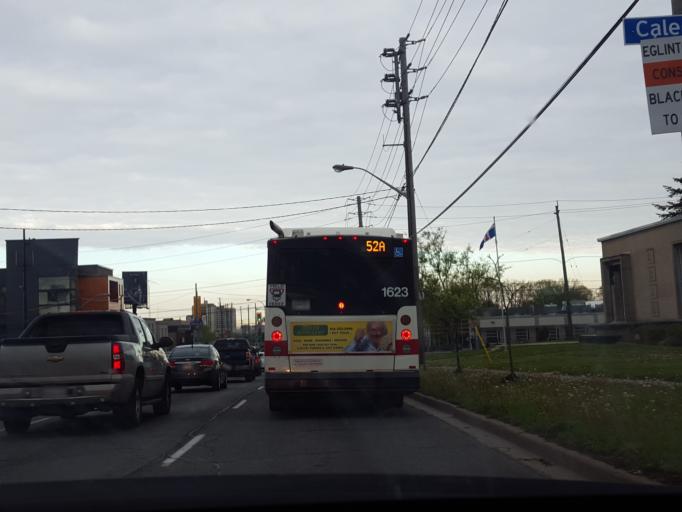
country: CA
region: Ontario
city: Toronto
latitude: 43.7118
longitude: -79.4656
